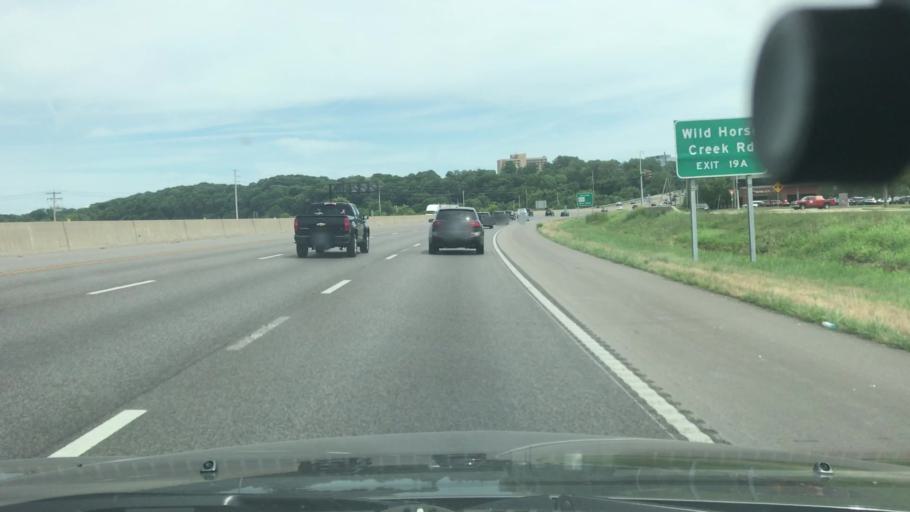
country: US
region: Missouri
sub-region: Saint Louis County
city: Chesterfield
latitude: 38.6684
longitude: -90.5785
